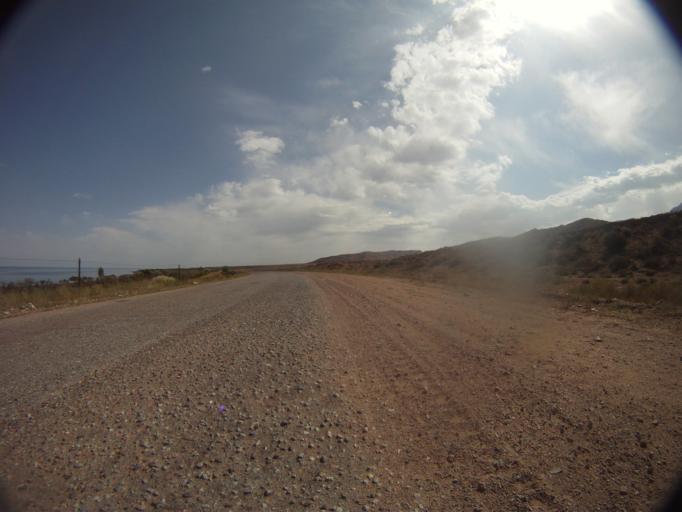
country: KG
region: Ysyk-Koel
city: Kadzhi-Say
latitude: 42.1720
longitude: 77.2639
